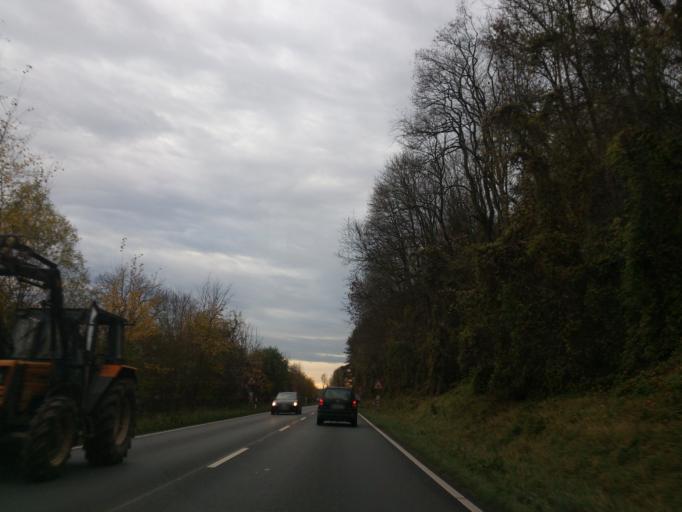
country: DE
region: Lower Saxony
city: Boffzen
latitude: 51.7609
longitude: 9.3753
